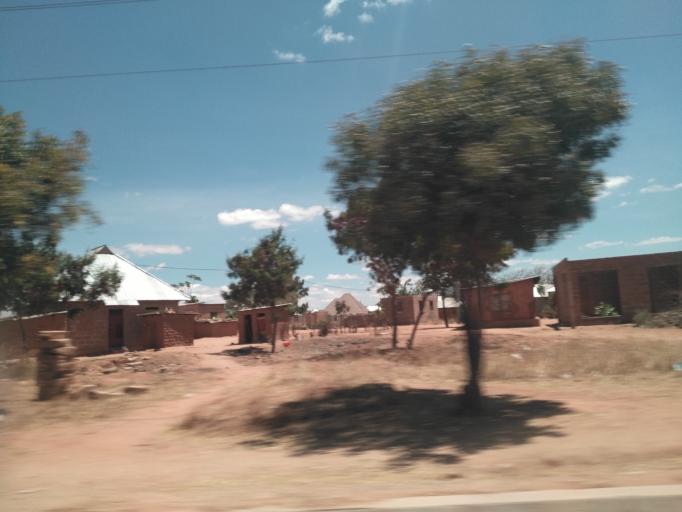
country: TZ
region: Dodoma
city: Kisasa
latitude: -6.1907
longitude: 35.7823
